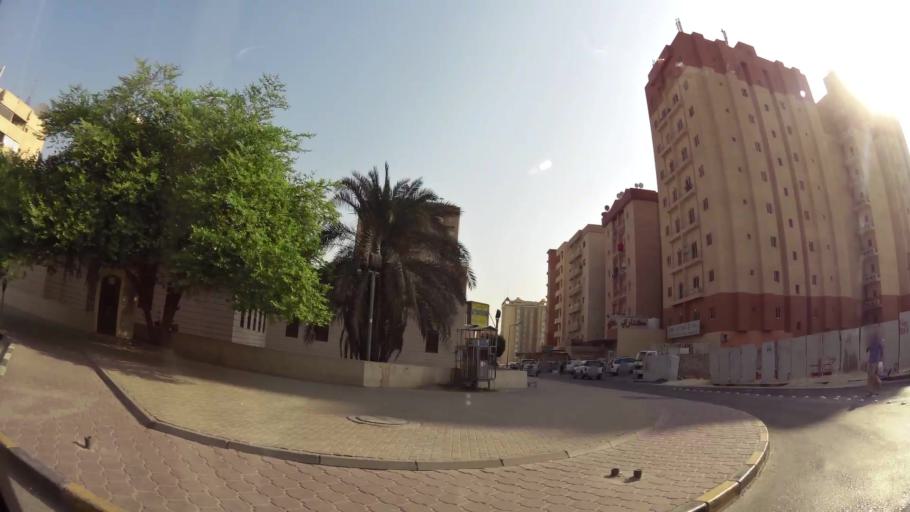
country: KW
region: Muhafazat Hawalli
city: Hawalli
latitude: 29.3328
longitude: 48.0270
